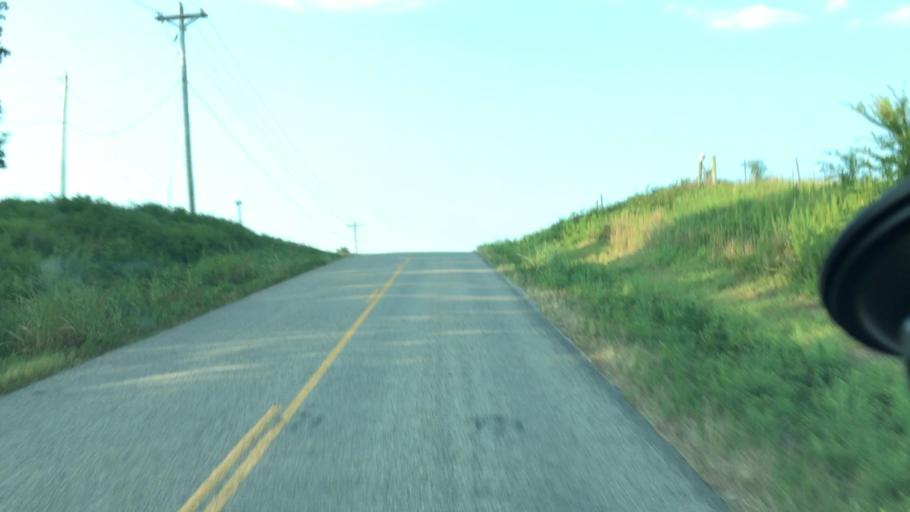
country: US
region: Arkansas
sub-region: Johnson County
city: Coal Hill
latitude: 35.3580
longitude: -93.6131
